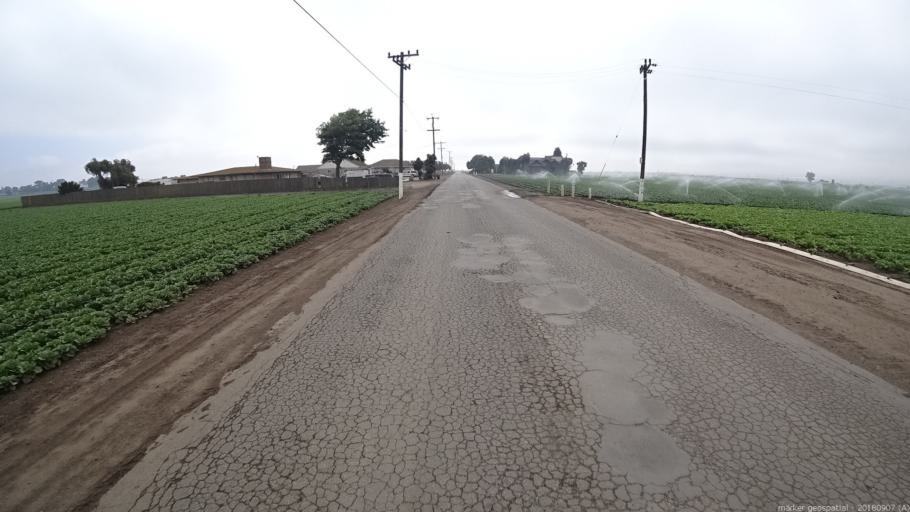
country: US
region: California
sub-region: Monterey County
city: Salinas
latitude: 36.6411
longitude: -121.6440
